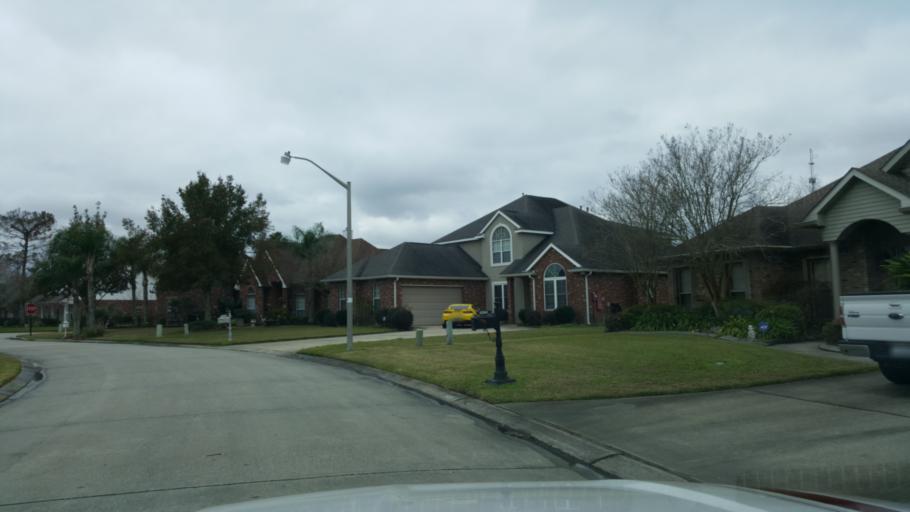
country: US
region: Louisiana
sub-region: Jefferson Parish
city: Woodmere
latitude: 29.8764
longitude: -90.0801
